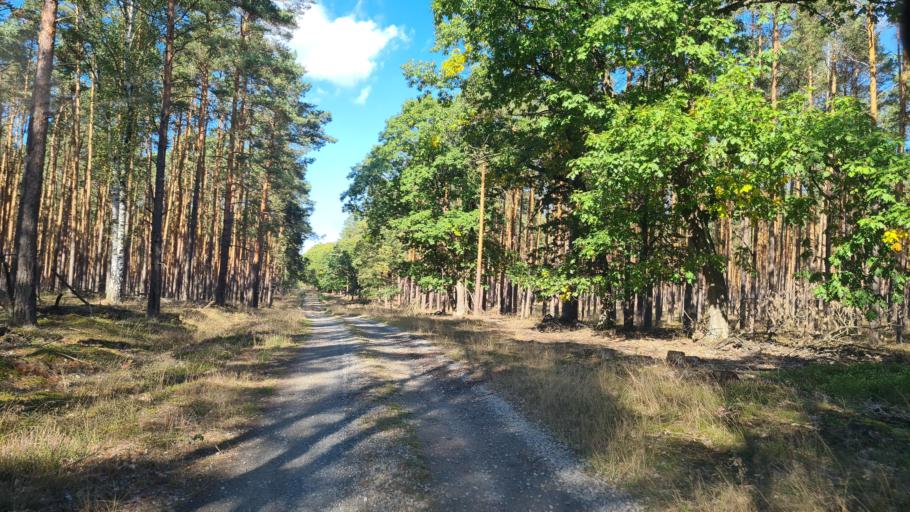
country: DE
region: Brandenburg
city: Hohenbucko
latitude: 51.8308
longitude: 13.5024
